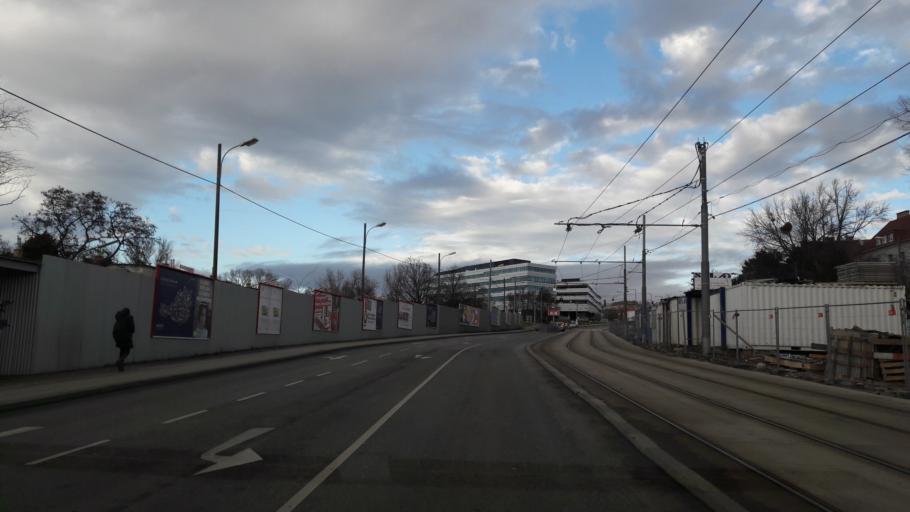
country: AT
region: Lower Austria
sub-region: Politischer Bezirk Wien-Umgebung
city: Leopoldsdorf
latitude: 48.1544
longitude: 16.3820
